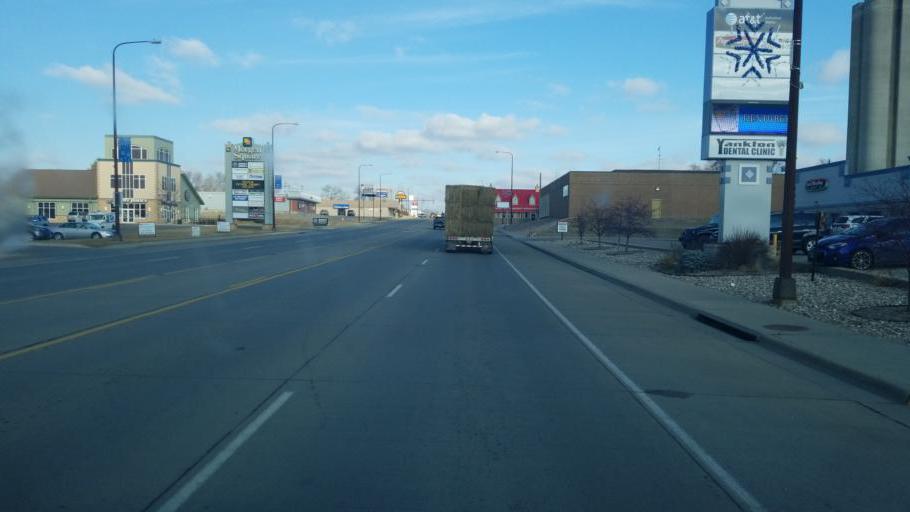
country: US
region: South Dakota
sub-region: Yankton County
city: Yankton
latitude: 42.8811
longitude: -97.3966
